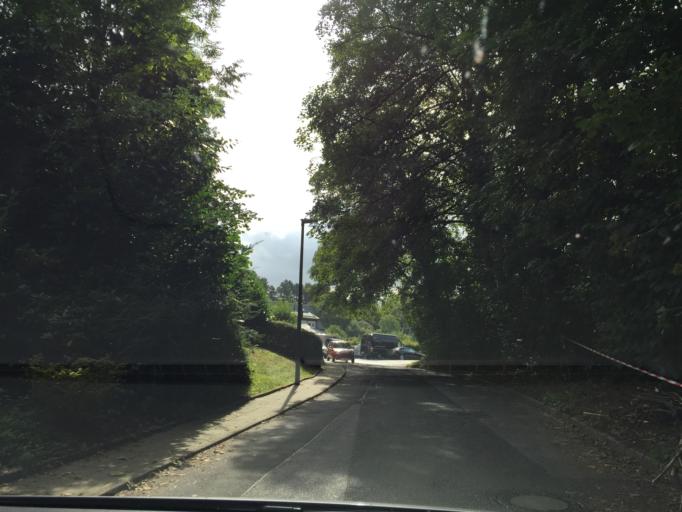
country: DE
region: North Rhine-Westphalia
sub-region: Regierungsbezirk Dusseldorf
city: Heiligenhaus
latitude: 51.3306
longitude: 6.9633
